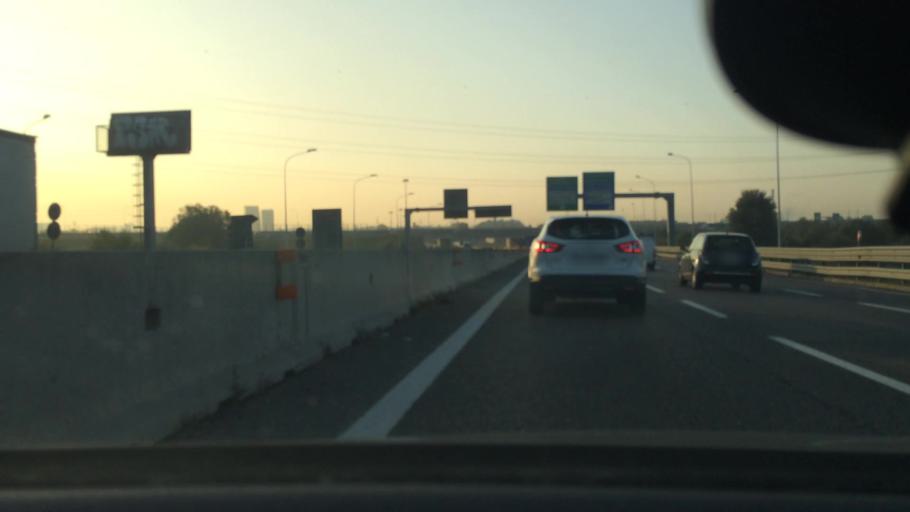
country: IT
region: Lombardy
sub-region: Citta metropolitana di Milano
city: Rho
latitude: 45.5271
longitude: 9.0576
